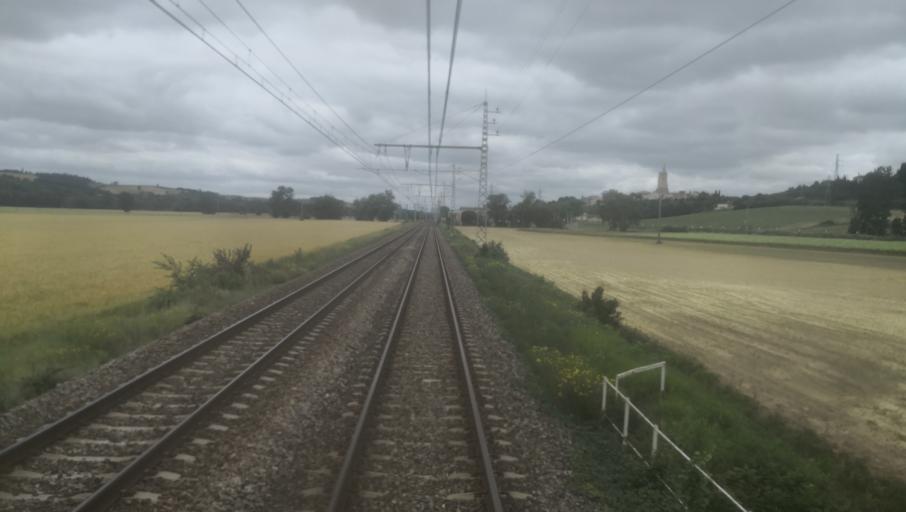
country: FR
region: Midi-Pyrenees
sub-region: Departement de la Haute-Garonne
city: Avignonet-Lauragais
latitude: 43.3610
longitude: 1.7985
